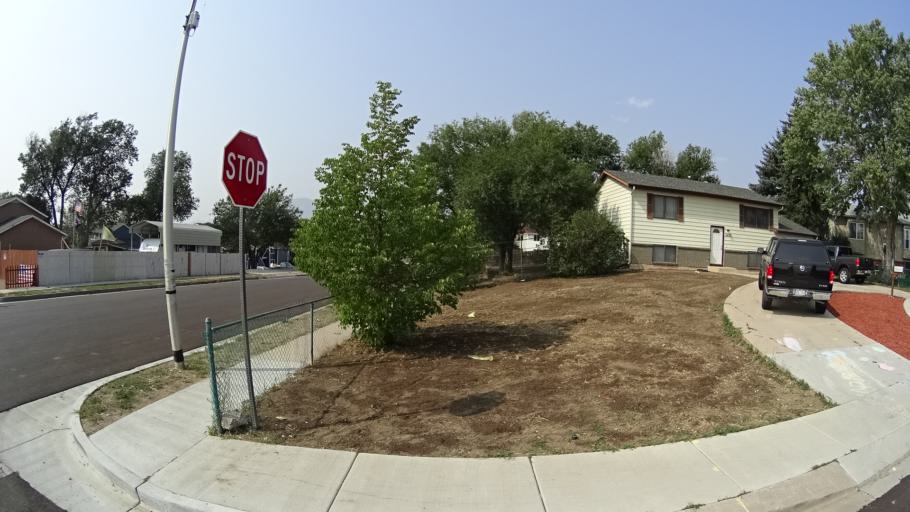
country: US
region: Colorado
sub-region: El Paso County
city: Stratmoor
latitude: 38.8105
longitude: -104.7648
